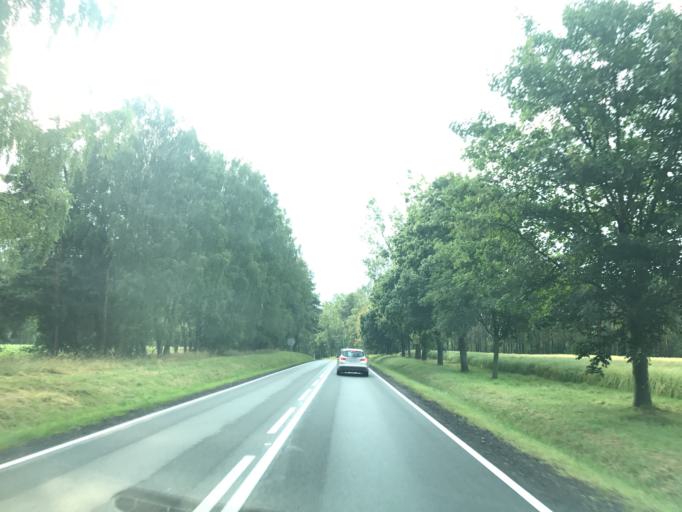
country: PL
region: Pomeranian Voivodeship
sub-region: Powiat czluchowski
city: Przechlewo
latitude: 53.7286
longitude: 17.2290
